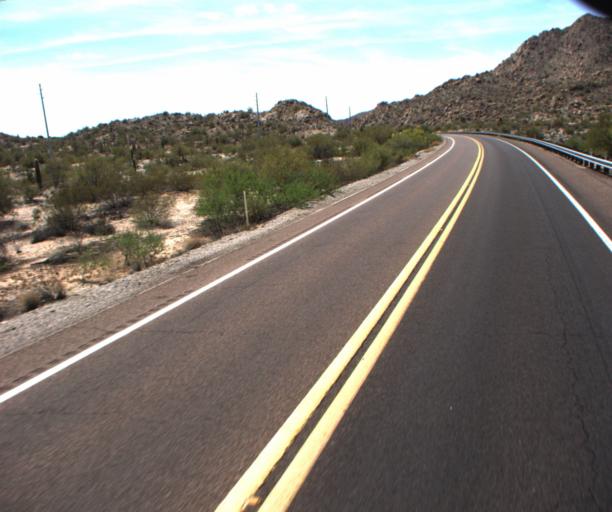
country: US
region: Arizona
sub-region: La Paz County
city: Salome
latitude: 33.7540
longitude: -113.6680
